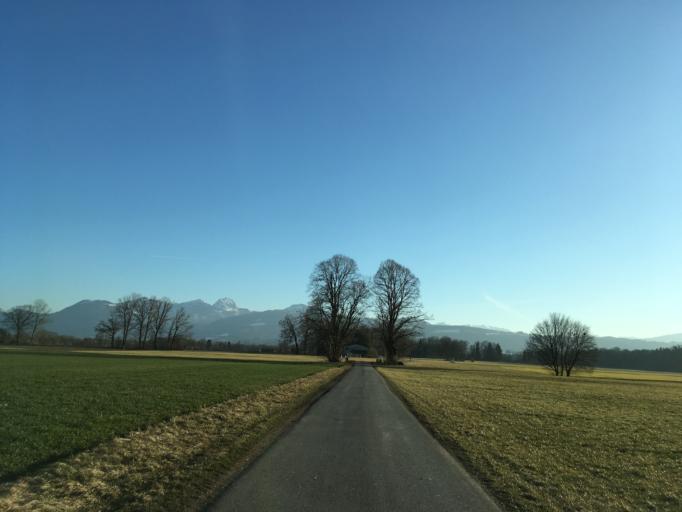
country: DE
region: Bavaria
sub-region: Upper Bavaria
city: Bad Aibling
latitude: 47.8401
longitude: 11.9922
